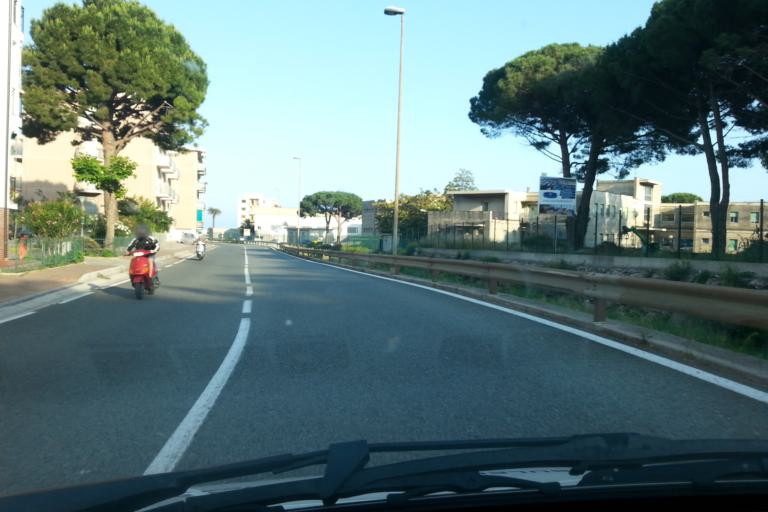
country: IT
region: Liguria
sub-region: Provincia di Savona
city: Pietra Ligure
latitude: 44.1457
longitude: 8.2722
